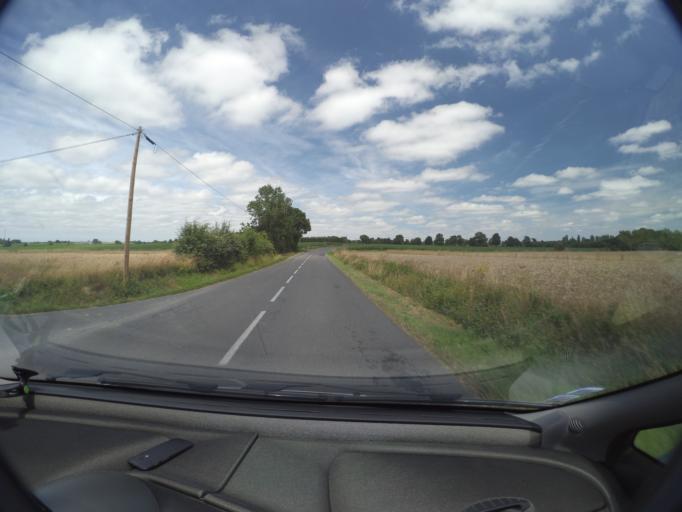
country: FR
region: Pays de la Loire
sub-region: Departement de la Loire-Atlantique
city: Saint-Hilaire-de-Clisson
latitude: 47.0467
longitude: -1.3227
